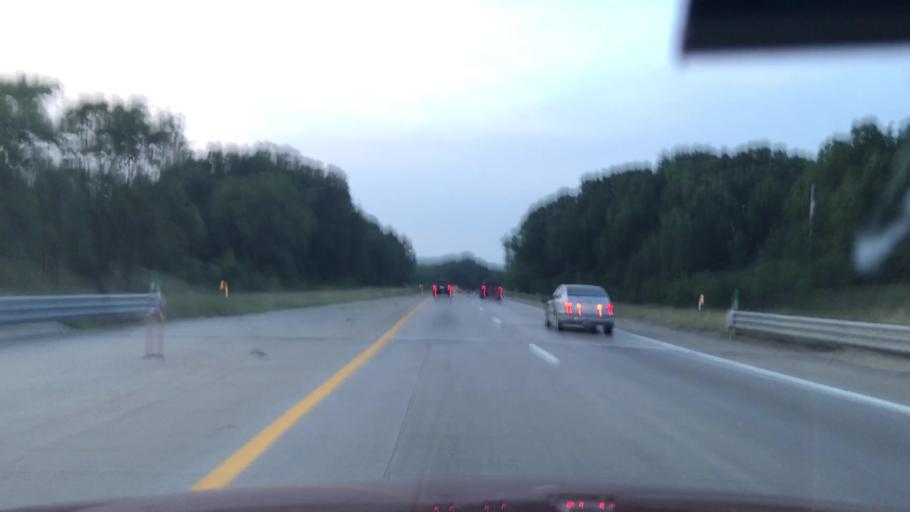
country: US
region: Michigan
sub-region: Kent County
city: Comstock Park
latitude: 43.0581
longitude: -85.6627
